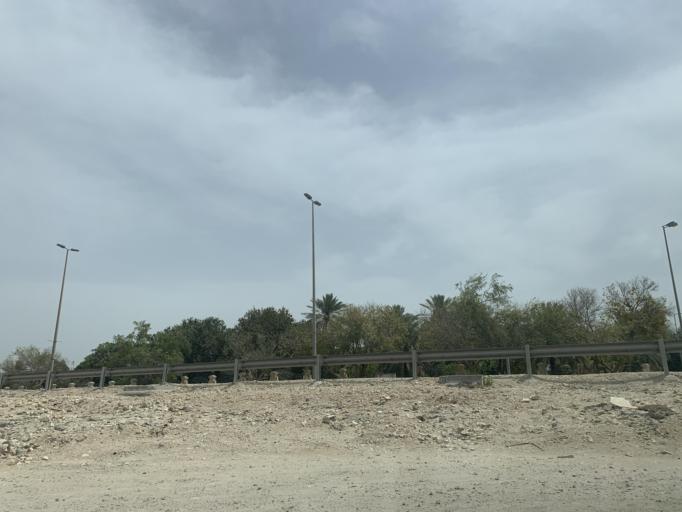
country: BH
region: Northern
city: Ar Rifa'
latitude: 26.1346
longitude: 50.5428
